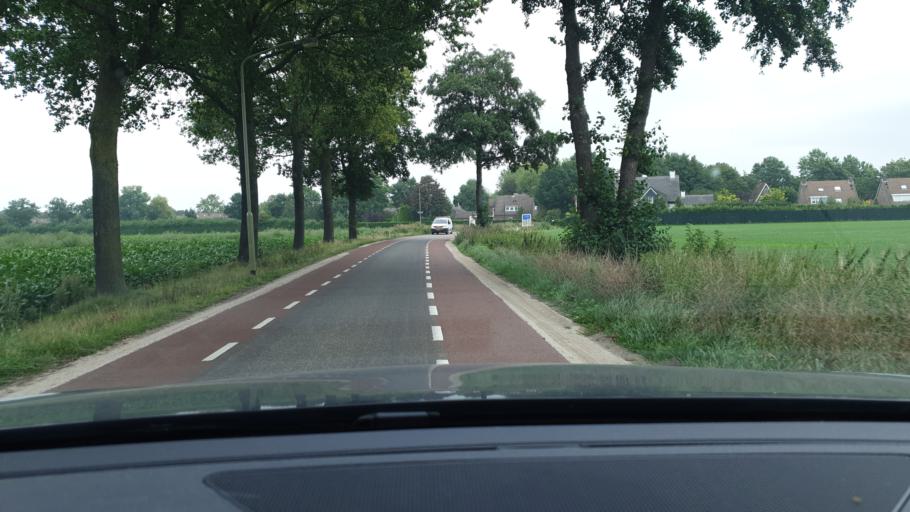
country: NL
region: North Brabant
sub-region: Gemeente Landerd
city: Schaijk
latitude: 51.7414
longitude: 5.6223
